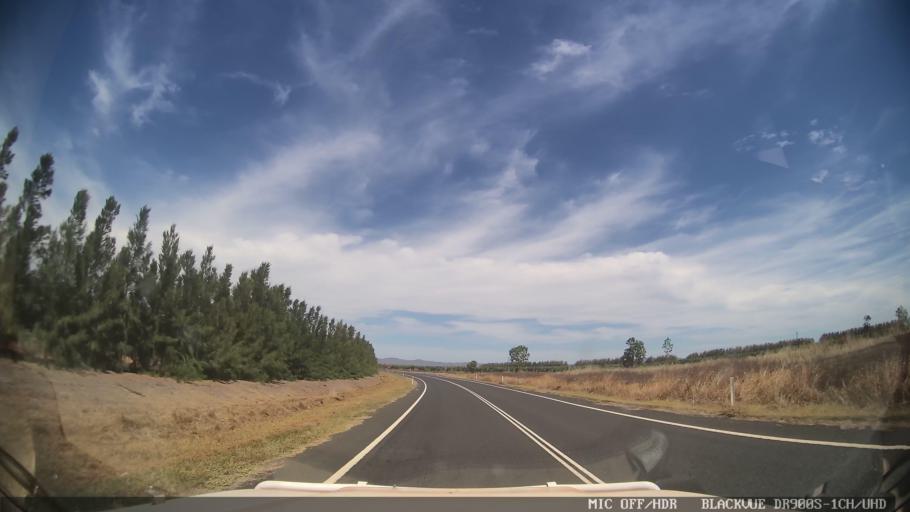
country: AU
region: Queensland
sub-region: Cook
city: Cooktown
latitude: -15.8339
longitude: 144.8545
